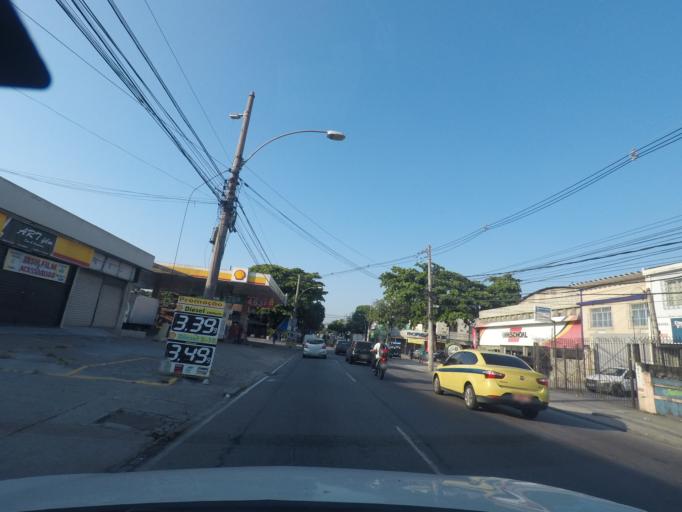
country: BR
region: Rio de Janeiro
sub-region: Duque De Caxias
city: Duque de Caxias
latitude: -22.8301
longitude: -43.2776
